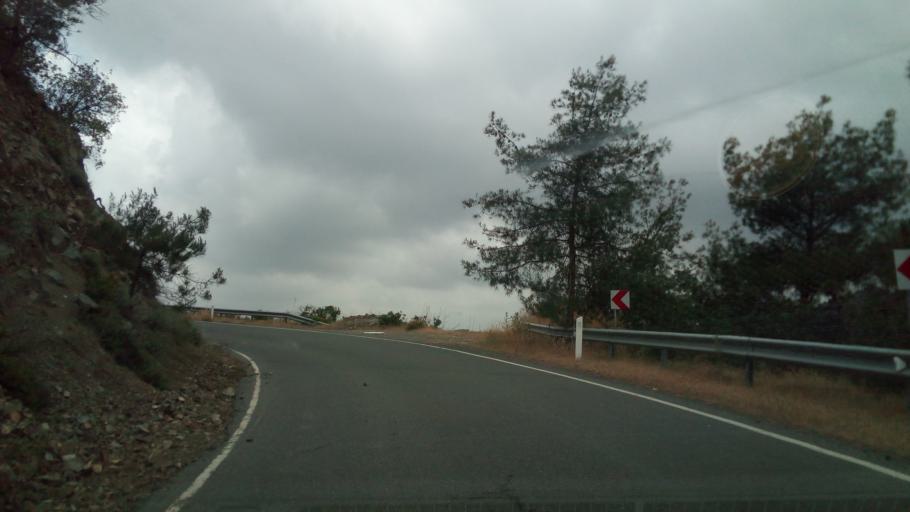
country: CY
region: Limassol
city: Pelendri
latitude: 34.8949
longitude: 32.9953
